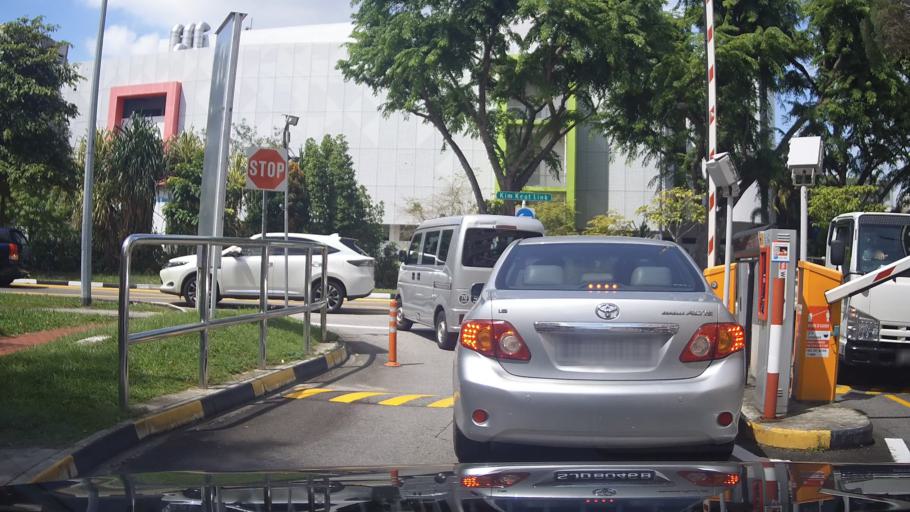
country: SG
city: Singapore
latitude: 1.3306
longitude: 103.8554
